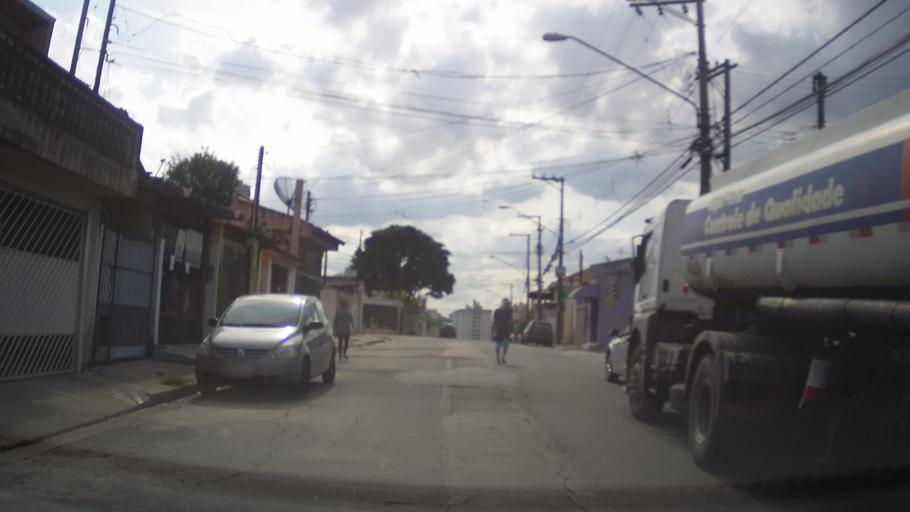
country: BR
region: Sao Paulo
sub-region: Guarulhos
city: Guarulhos
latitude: -23.4567
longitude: -46.5071
